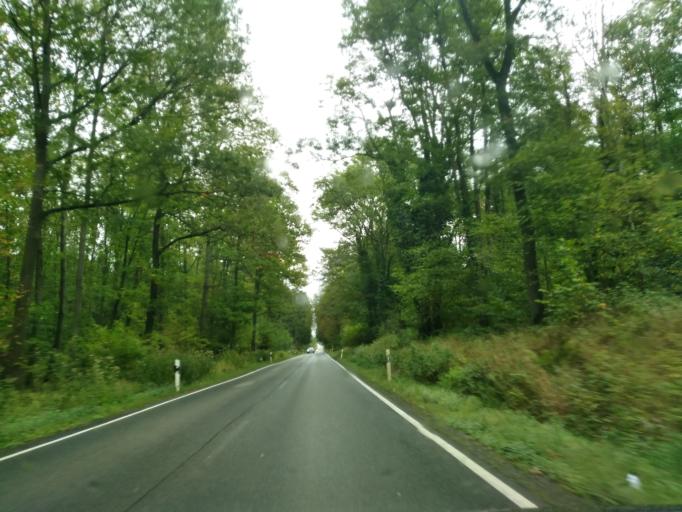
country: DE
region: Rheinland-Pfalz
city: Windhagen
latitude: 50.6557
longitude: 7.3423
